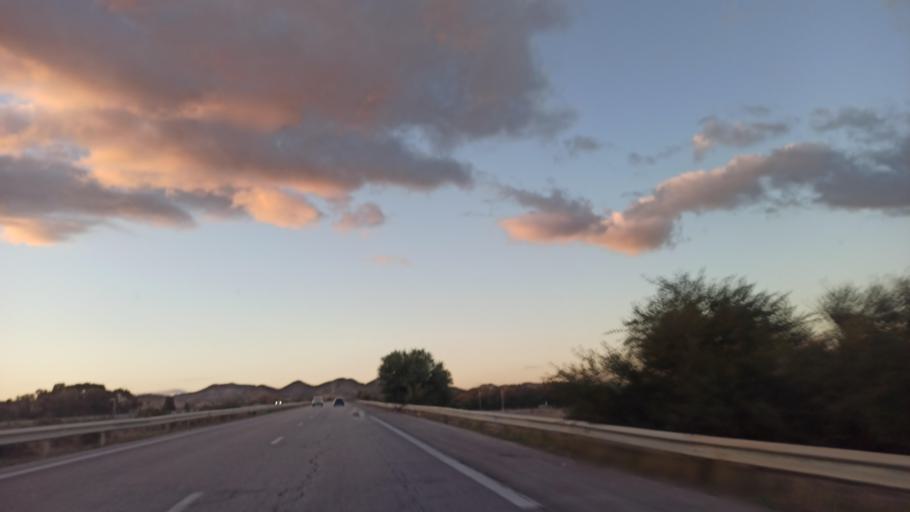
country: TN
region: Susah
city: Harqalah
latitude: 36.2116
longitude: 10.4255
